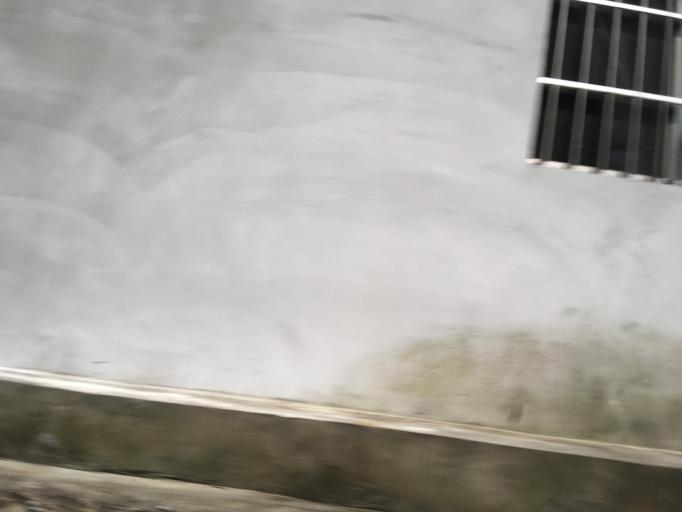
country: TW
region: Taipei
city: Taipei
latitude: 24.9478
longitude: 121.5565
